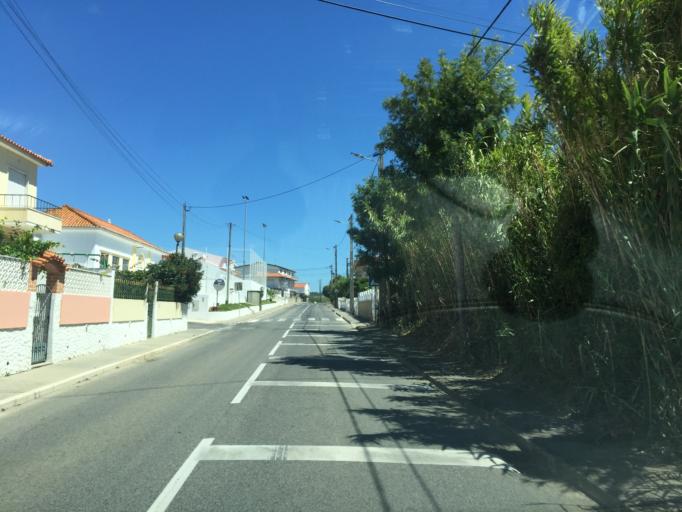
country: PT
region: Lisbon
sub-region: Torres Vedras
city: A dos Cunhados
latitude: 39.1815
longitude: -9.3145
